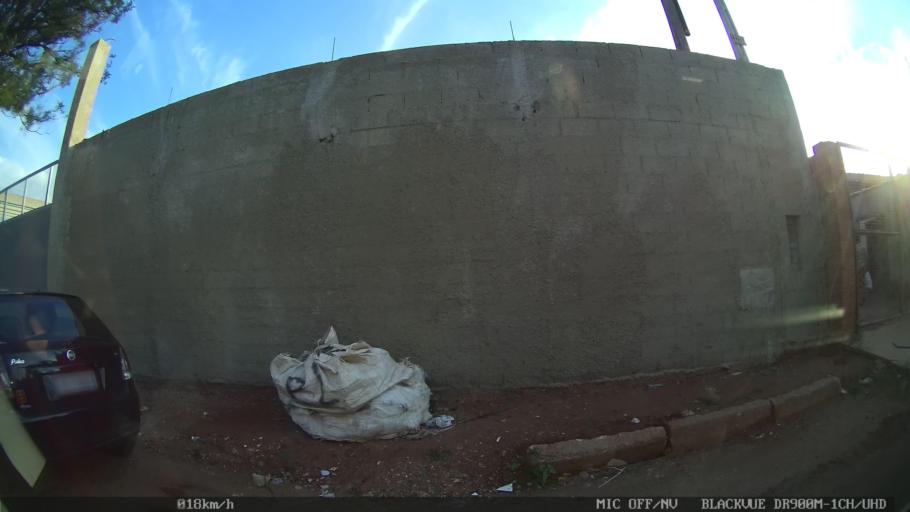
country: BR
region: Sao Paulo
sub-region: Hortolandia
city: Hortolandia
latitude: -22.8654
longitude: -47.1491
